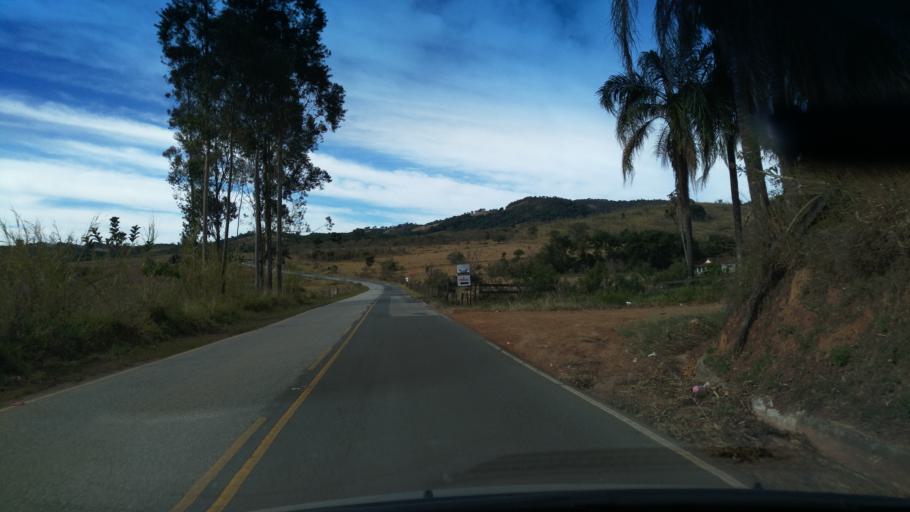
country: BR
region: Minas Gerais
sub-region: Andradas
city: Andradas
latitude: -22.0566
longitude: -46.3970
